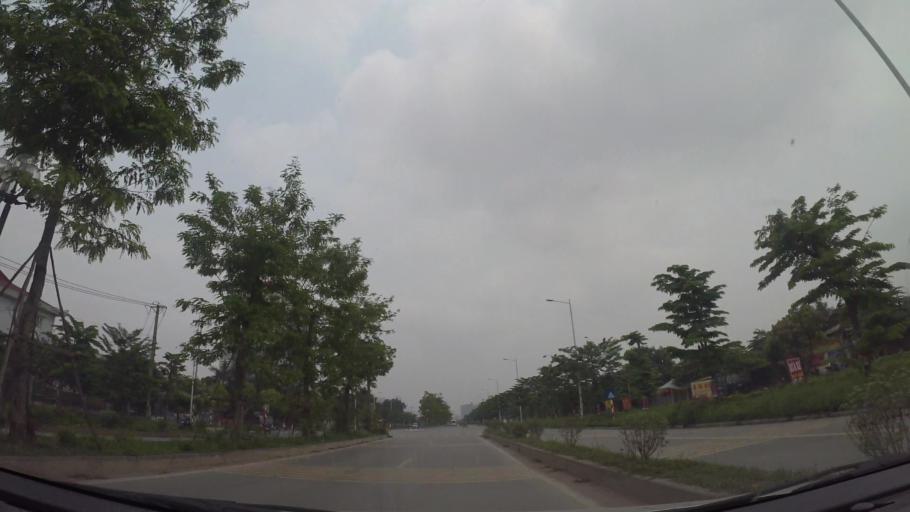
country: VN
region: Ha Noi
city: Cau Dien
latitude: 21.0399
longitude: 105.7408
